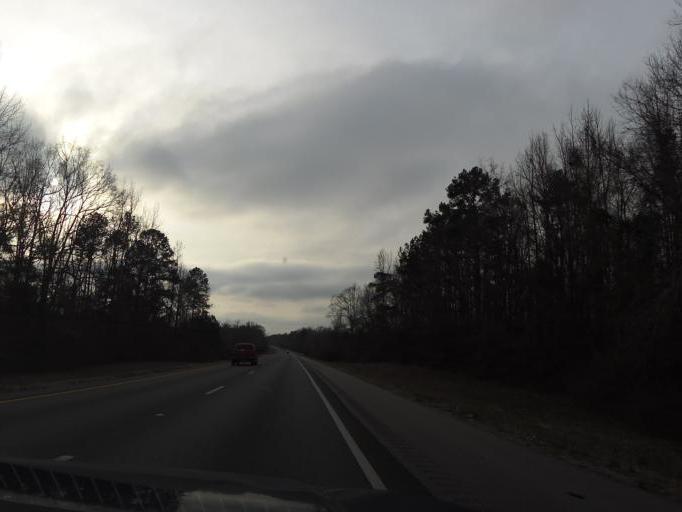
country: US
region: Alabama
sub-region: Chilton County
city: Clanton
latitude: 32.7825
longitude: -86.5731
